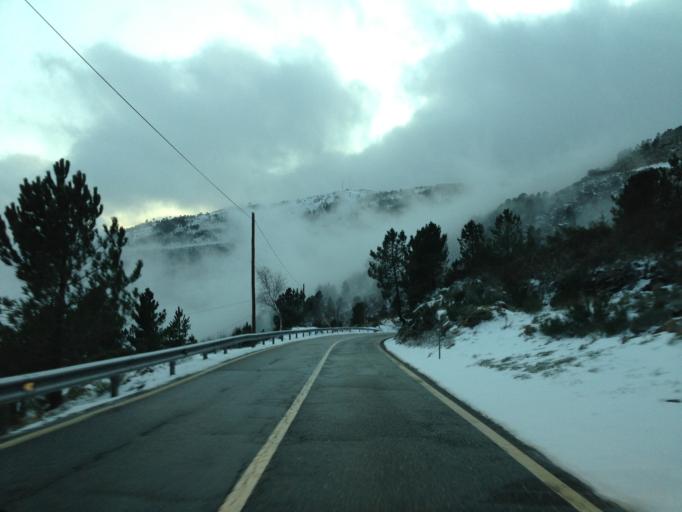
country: PT
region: Castelo Branco
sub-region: Covilha
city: Covilha
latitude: 40.2908
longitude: -7.5302
